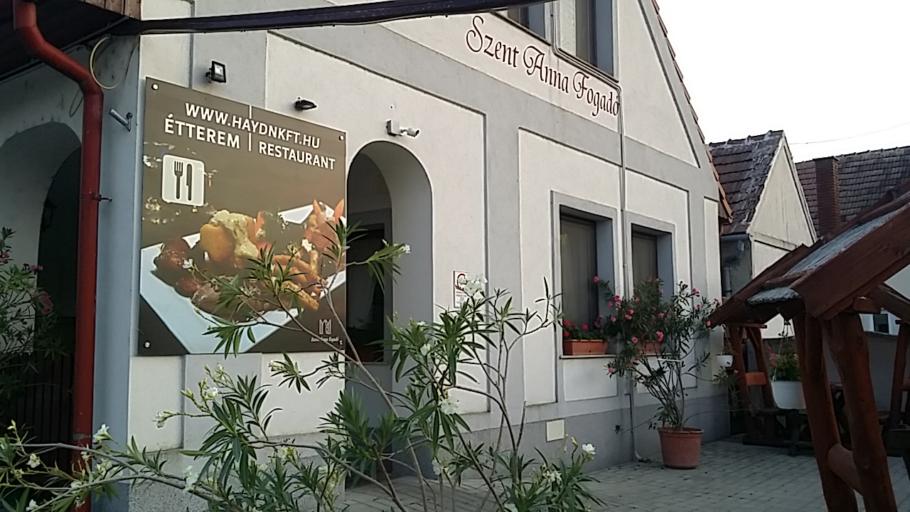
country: HU
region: Gyor-Moson-Sopron
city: Nagycenk
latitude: 47.6215
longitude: 16.7759
